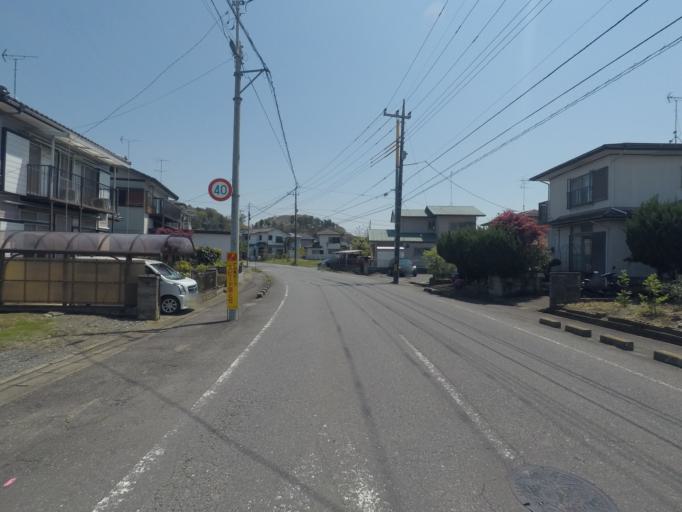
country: JP
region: Ibaraki
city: Ushiku
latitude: 35.9892
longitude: 140.1094
